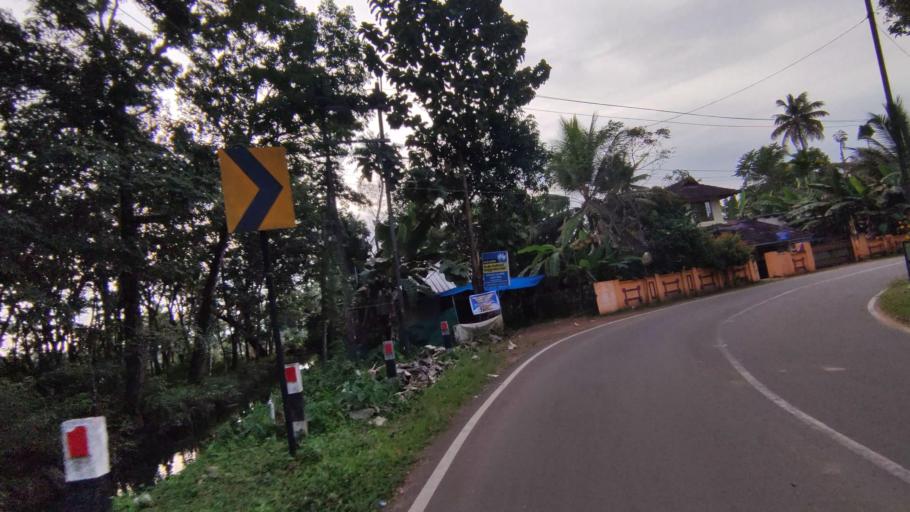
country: IN
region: Kerala
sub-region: Kottayam
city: Kottayam
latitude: 9.6374
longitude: 76.4893
